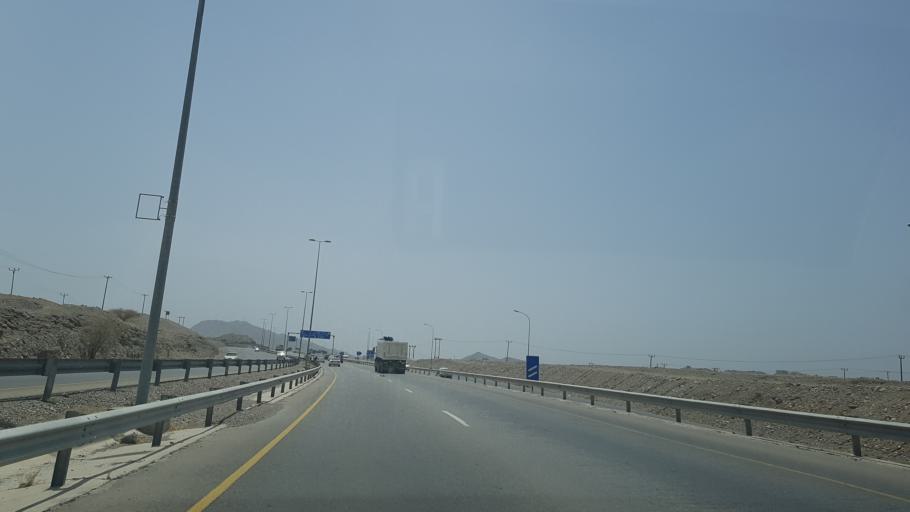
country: OM
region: Muhafazat ad Dakhiliyah
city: Bidbid
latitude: 23.4386
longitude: 58.1202
